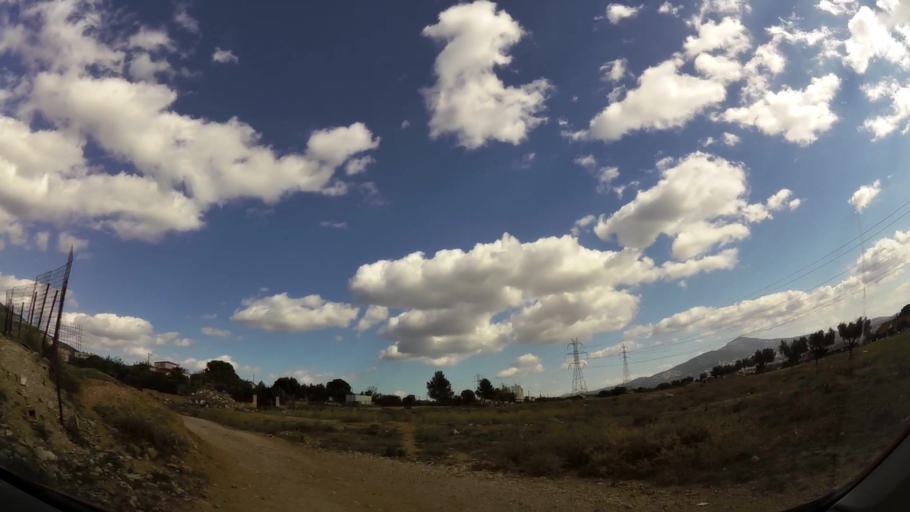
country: GR
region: Attica
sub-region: Nomarchia Anatolikis Attikis
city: Thrakomakedones
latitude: 38.1111
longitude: 23.7509
